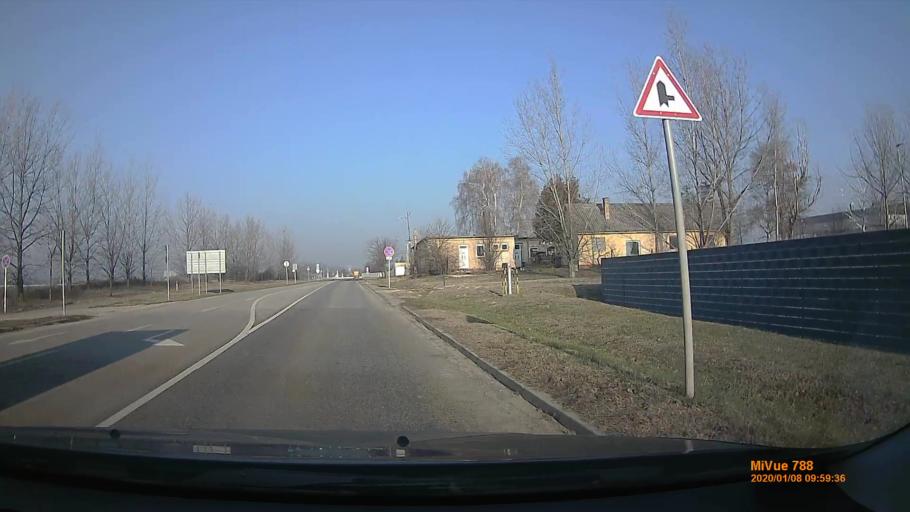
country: HU
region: Bacs-Kiskun
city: Kecskemet
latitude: 46.8723
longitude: 19.7015
